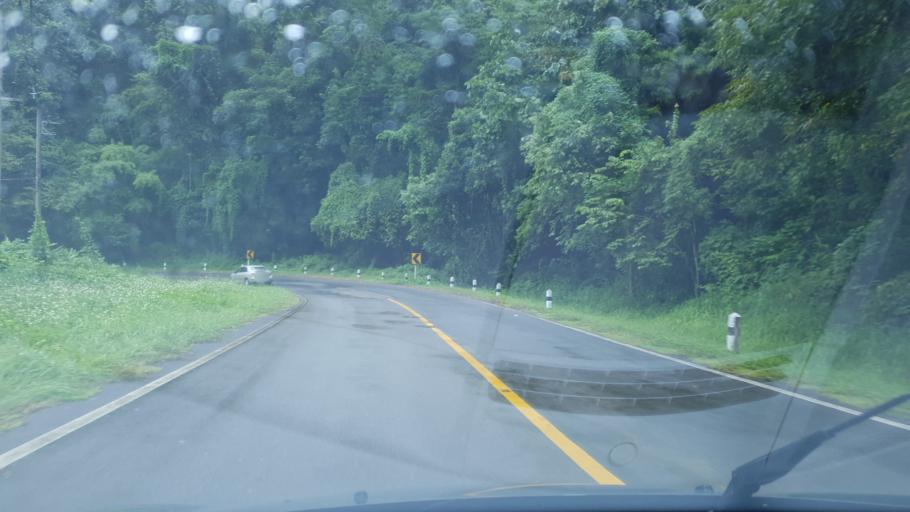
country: TH
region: Mae Hong Son
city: Mae La Noi
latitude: 18.5761
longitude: 97.9395
